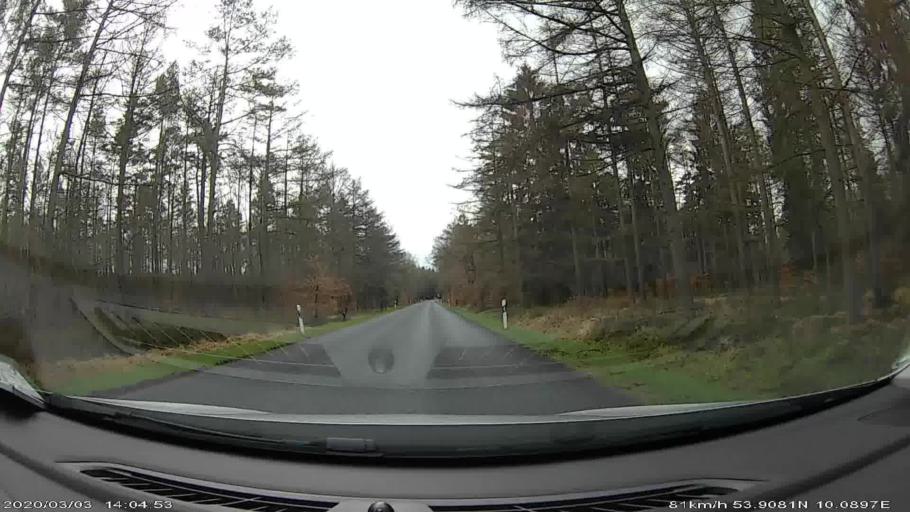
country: DE
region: Schleswig-Holstein
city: Hartenholm
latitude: 53.9074
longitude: 10.0892
